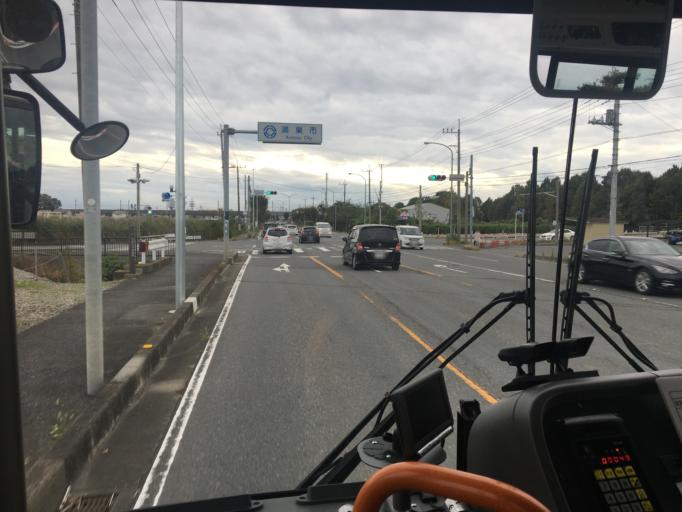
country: JP
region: Saitama
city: Fukiage-fujimi
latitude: 36.1159
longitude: 139.4606
